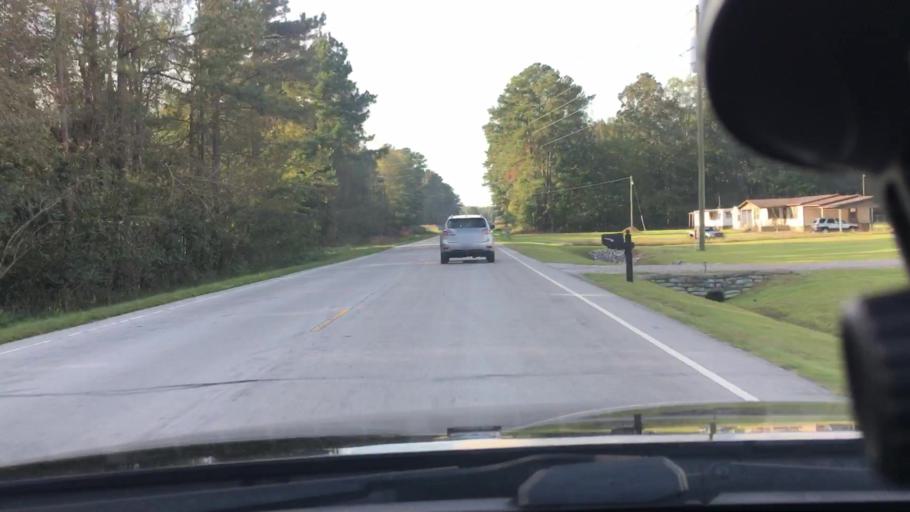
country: US
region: North Carolina
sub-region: Pitt County
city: Windsor
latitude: 35.4784
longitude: -77.2973
